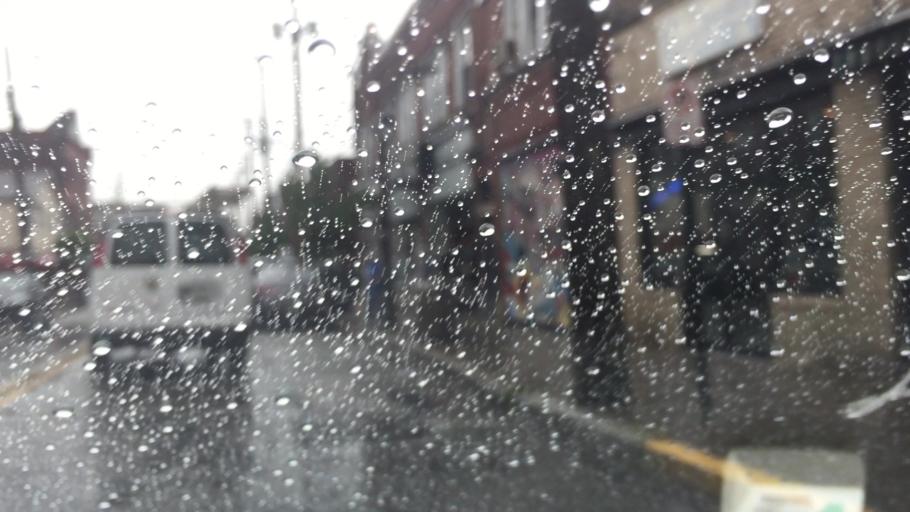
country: US
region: Pennsylvania
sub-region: Allegheny County
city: Millvale
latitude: 40.4808
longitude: -79.9749
